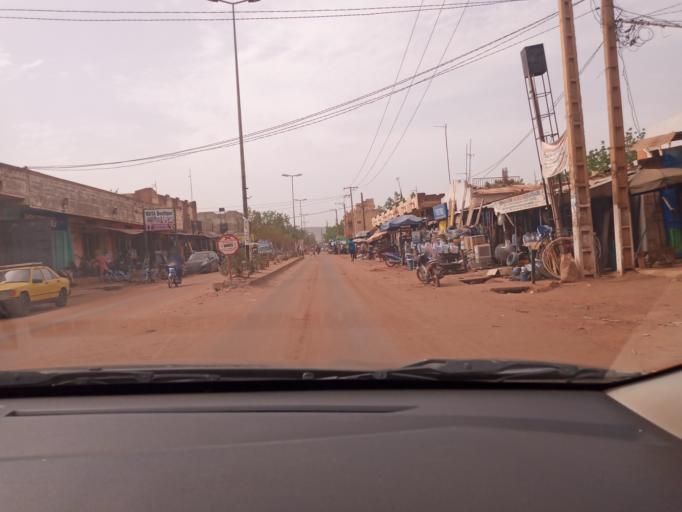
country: ML
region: Bamako
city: Bamako
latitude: 12.6747
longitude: -7.9242
